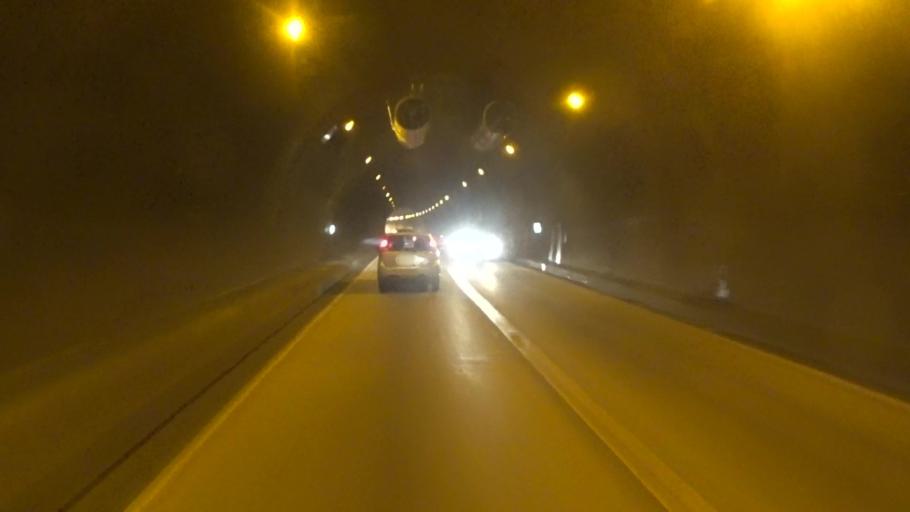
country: JP
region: Kyoto
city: Miyazu
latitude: 35.5495
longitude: 135.1751
